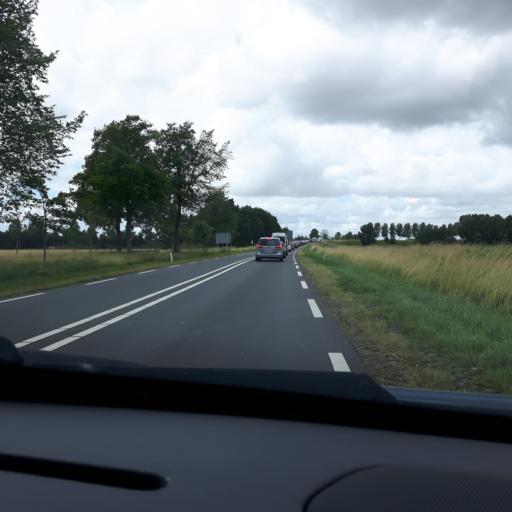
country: NL
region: Zeeland
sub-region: Gemeente Goes
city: Goes
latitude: 51.5126
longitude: 3.8692
